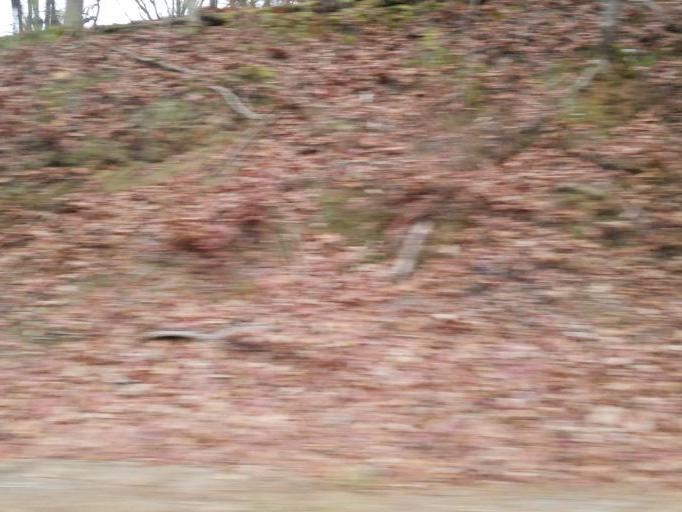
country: US
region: Georgia
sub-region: Dawson County
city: Dawsonville
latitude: 34.4337
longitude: -84.0771
